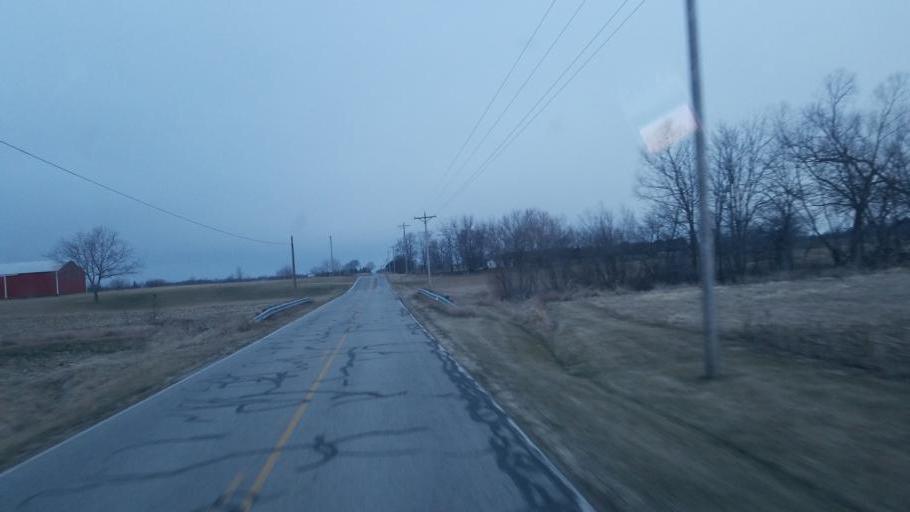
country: US
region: Ohio
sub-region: Defiance County
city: Hicksville
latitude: 41.3250
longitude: -84.7317
